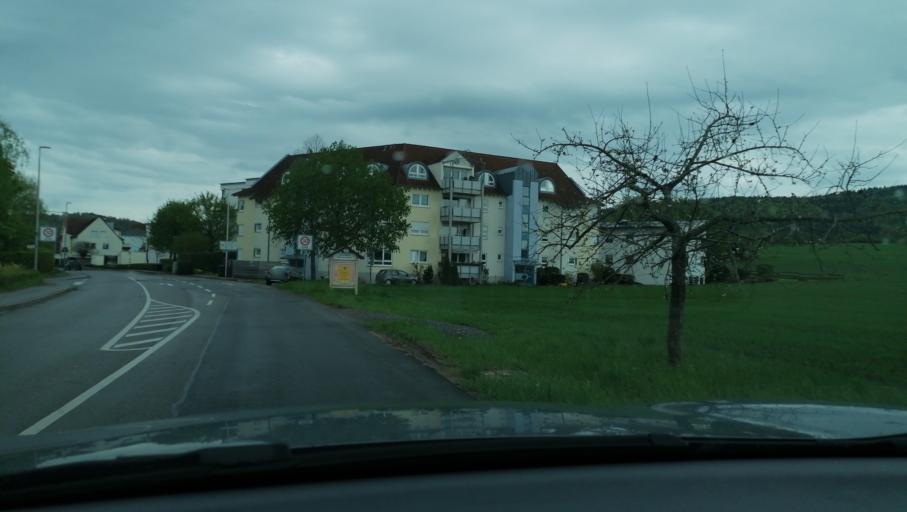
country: DE
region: Baden-Wuerttemberg
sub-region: Regierungsbezirk Stuttgart
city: Winnenden
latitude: 48.8668
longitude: 9.4246
